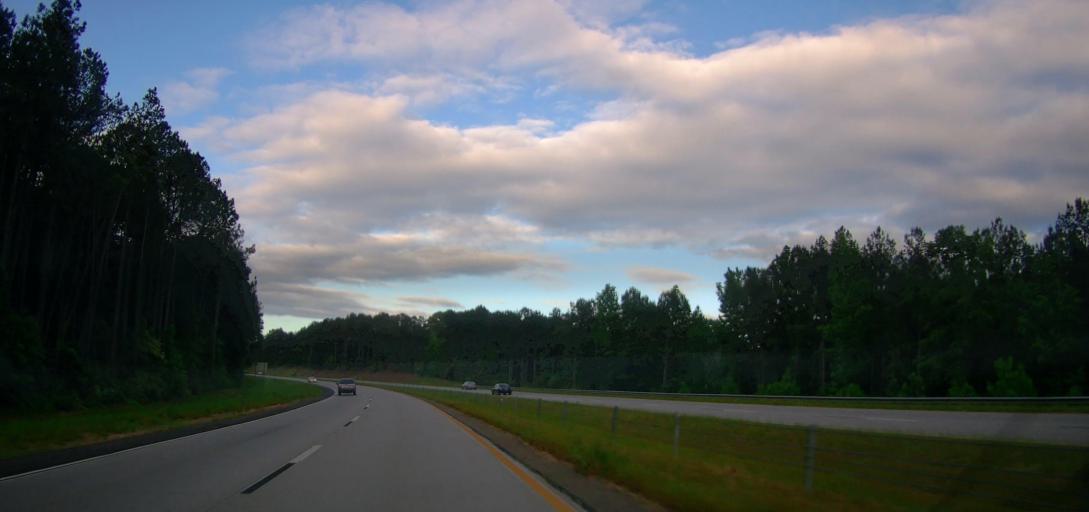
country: US
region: Georgia
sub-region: Oconee County
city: Watkinsville
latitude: 33.9093
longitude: -83.4363
